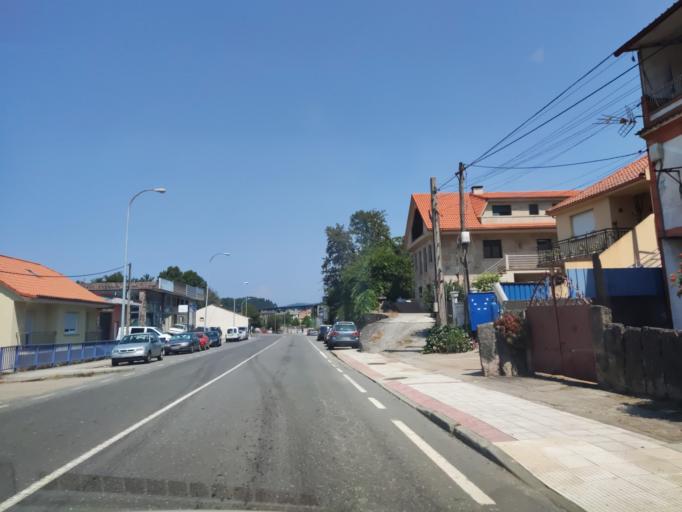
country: ES
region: Galicia
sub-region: Provincia de Pontevedra
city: Redondela
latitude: 42.2755
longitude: -8.6102
